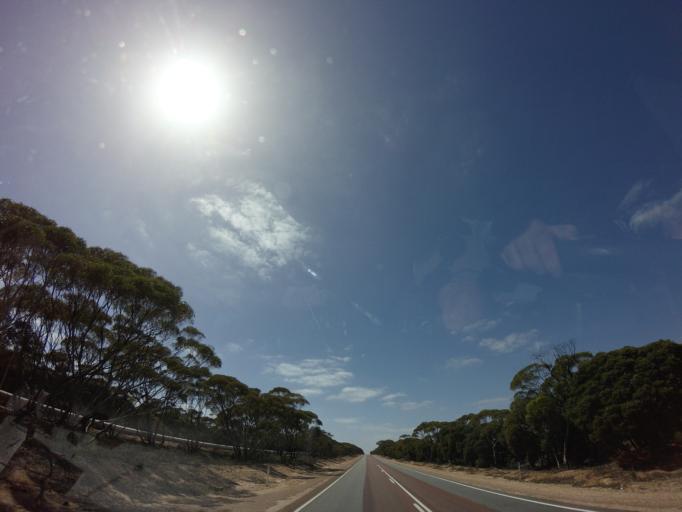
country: AU
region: South Australia
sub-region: Kimba
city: Caralue
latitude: -33.0931
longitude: 135.5145
